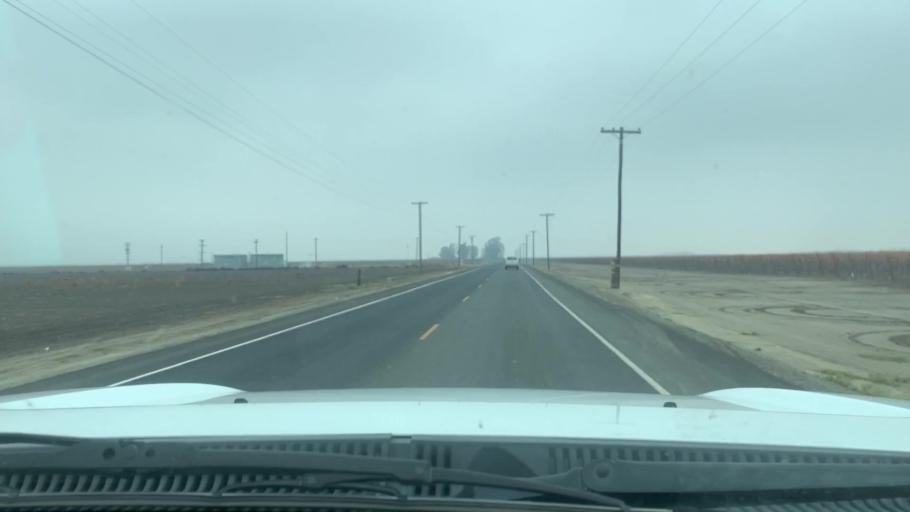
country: US
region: California
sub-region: Kern County
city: Lost Hills
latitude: 35.4994
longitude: -119.5945
